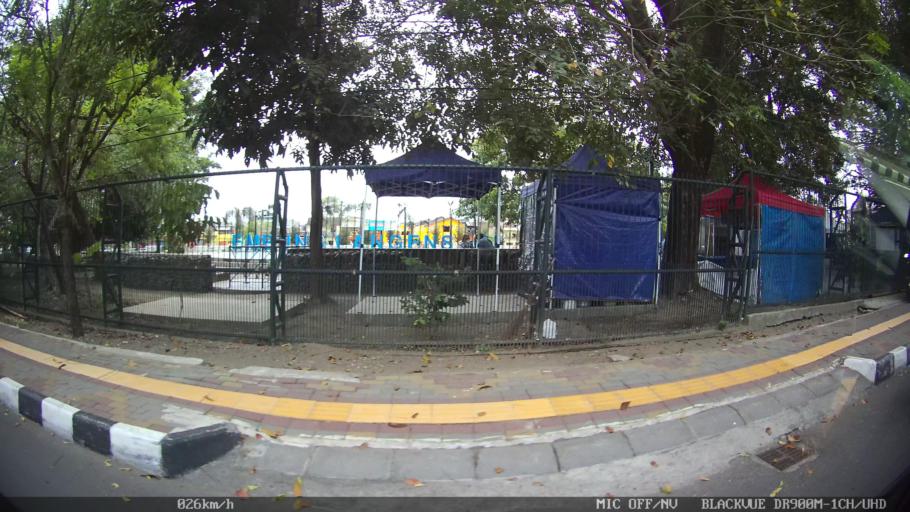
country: ID
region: Daerah Istimewa Yogyakarta
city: Yogyakarta
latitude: -7.7868
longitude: 110.3821
